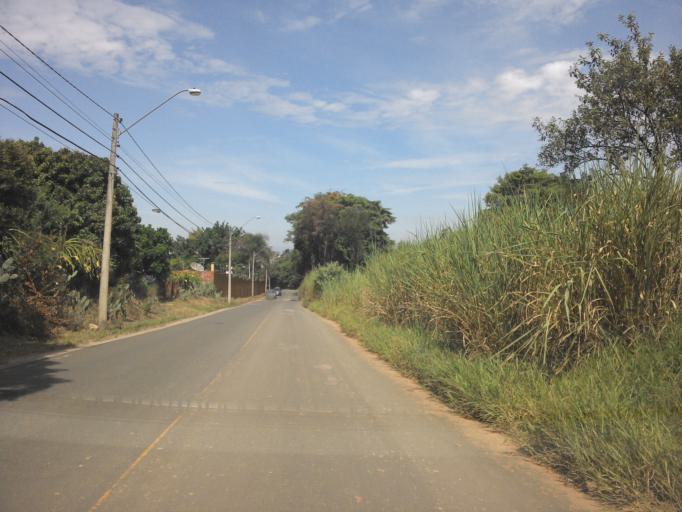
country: BR
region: Sao Paulo
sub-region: Valinhos
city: Valinhos
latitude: -22.9376
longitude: -46.9846
